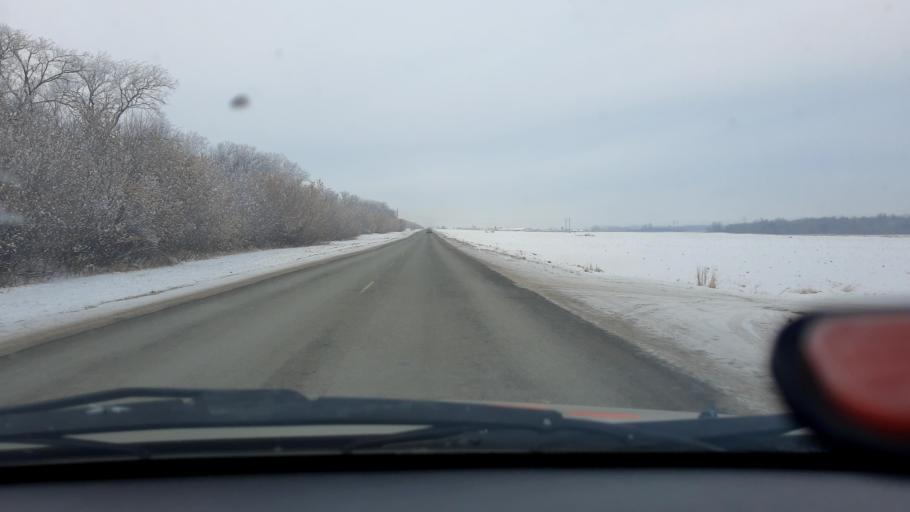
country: RU
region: Bashkortostan
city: Avdon
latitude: 54.3952
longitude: 55.8055
